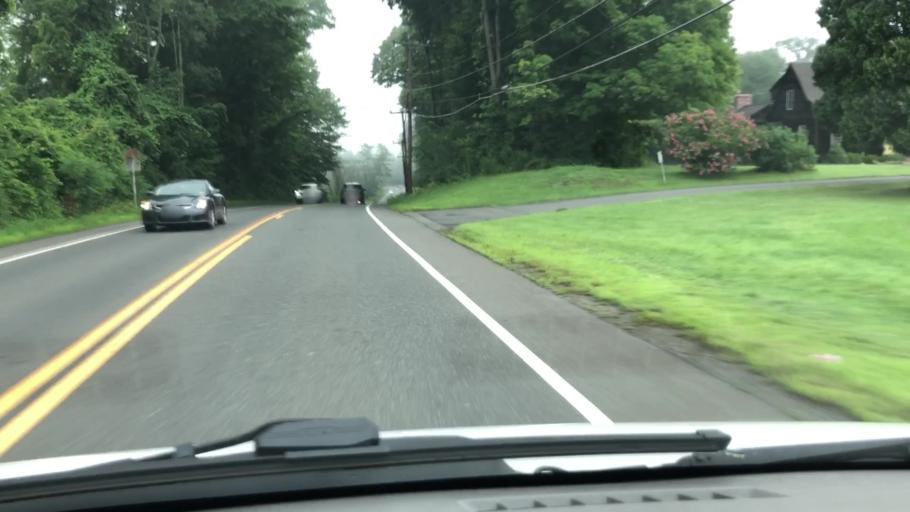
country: US
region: Massachusetts
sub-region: Franklin County
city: South Deerfield
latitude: 42.5123
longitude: -72.6057
